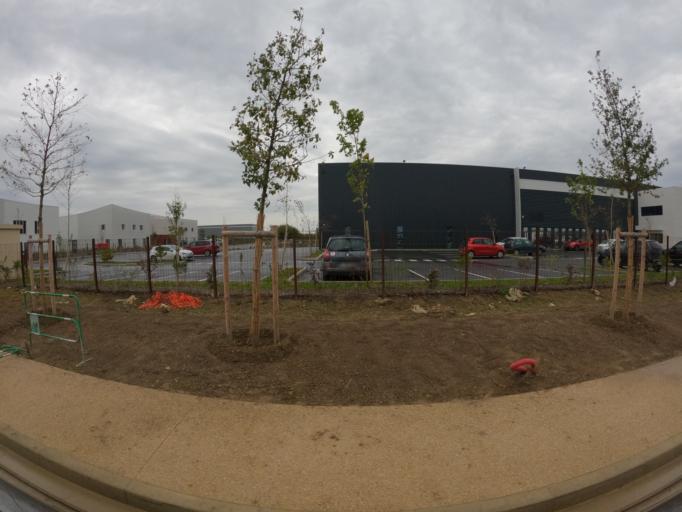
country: FR
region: Ile-de-France
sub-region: Departement de Seine-et-Marne
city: Serris
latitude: 48.8404
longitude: 2.7985
